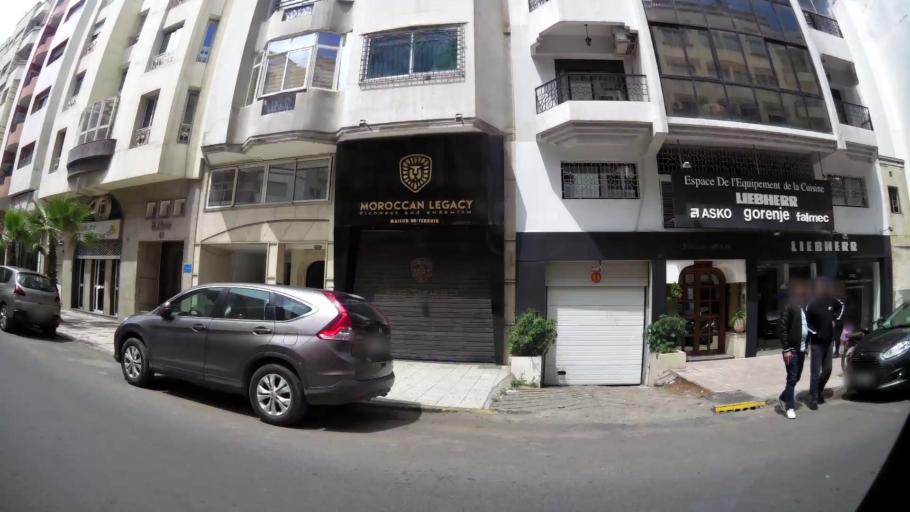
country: MA
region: Grand Casablanca
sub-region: Casablanca
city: Casablanca
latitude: 33.5946
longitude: -7.6414
